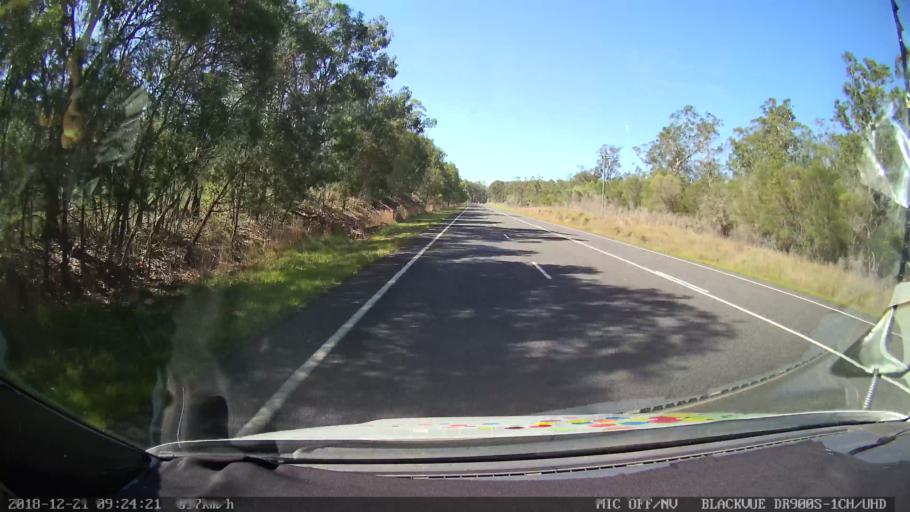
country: AU
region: New South Wales
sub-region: Clarence Valley
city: Maclean
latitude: -29.3662
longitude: 153.0165
